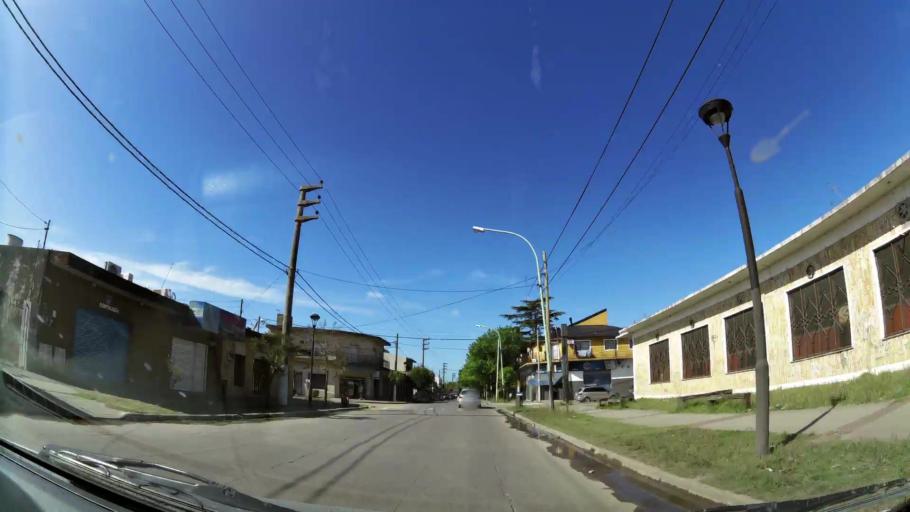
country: AR
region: Buenos Aires
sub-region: Partido de Quilmes
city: Quilmes
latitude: -34.8043
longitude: -58.2228
